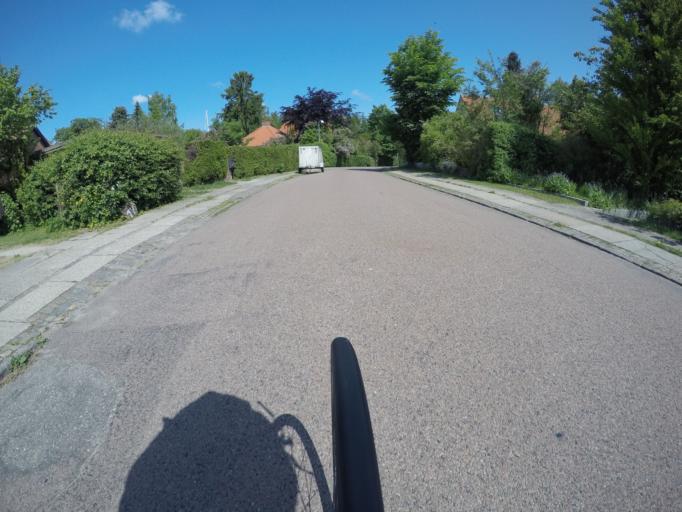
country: DK
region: Capital Region
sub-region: Rudersdal Kommune
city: Holte
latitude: 55.8001
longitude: 12.4681
